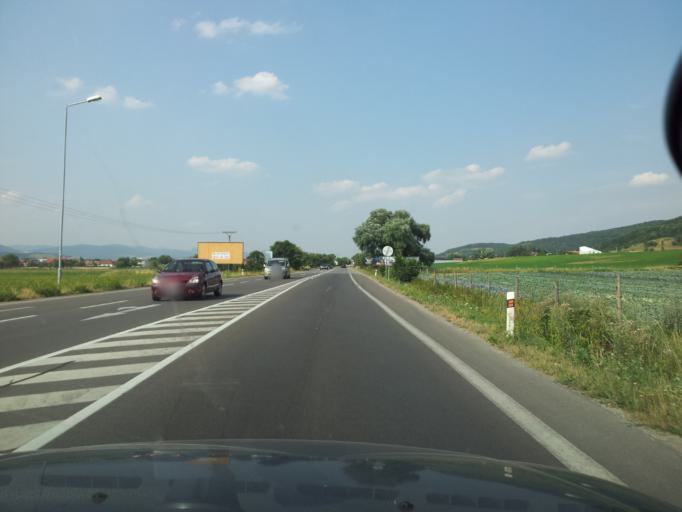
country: SK
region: Trenciansky
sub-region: Okres Trencin
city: Trencin
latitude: 48.9049
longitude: 18.0901
